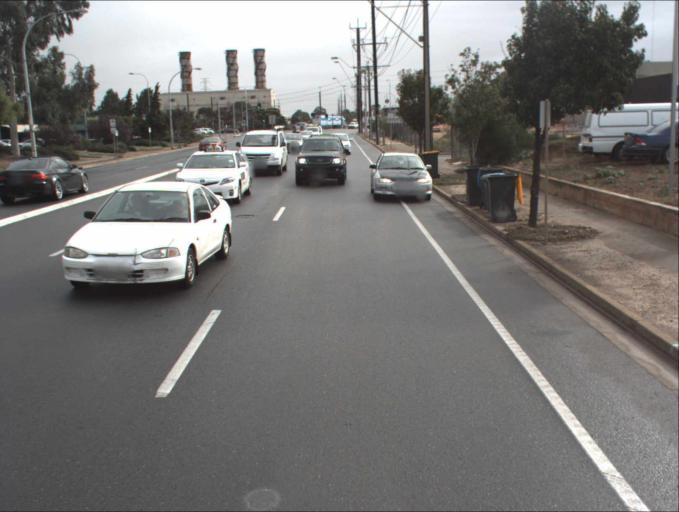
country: AU
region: South Australia
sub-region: Port Adelaide Enfield
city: Blair Athol
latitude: -34.8511
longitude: 138.5825
